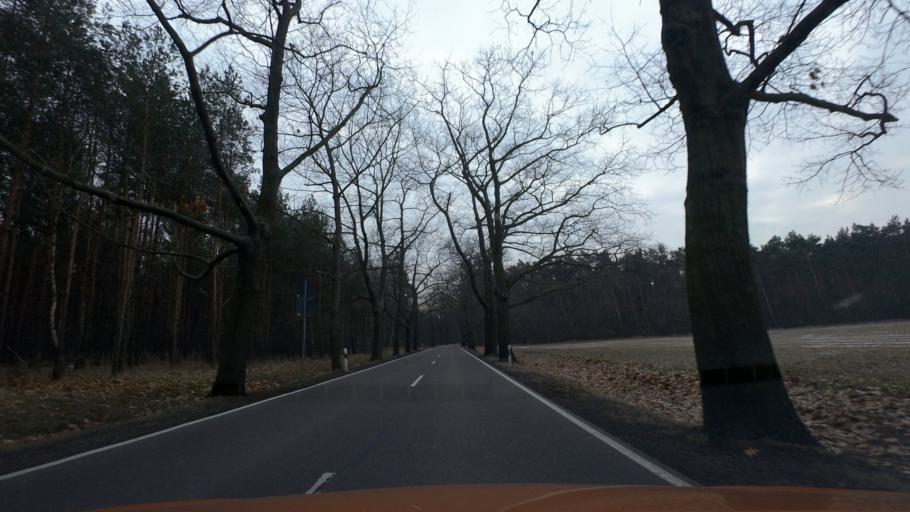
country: DE
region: Brandenburg
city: Ludwigsfelde
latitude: 52.2726
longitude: 13.2193
